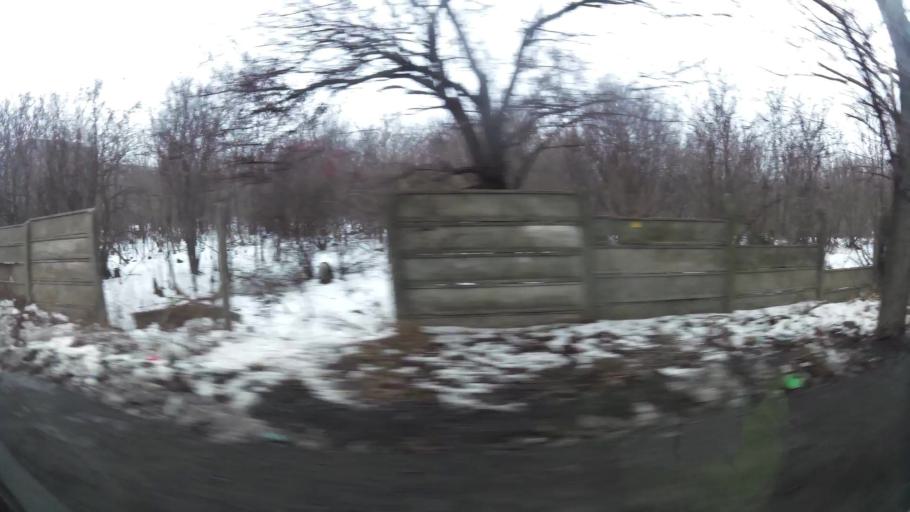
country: RO
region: Ilfov
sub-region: Comuna Chiajna
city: Chiajna
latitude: 44.4321
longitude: 25.9674
